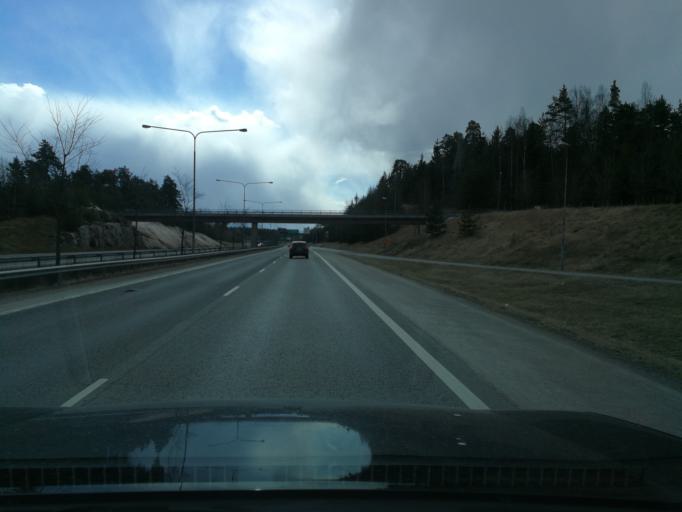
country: FI
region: Varsinais-Suomi
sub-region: Turku
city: Turku
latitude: 60.4354
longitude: 22.3201
